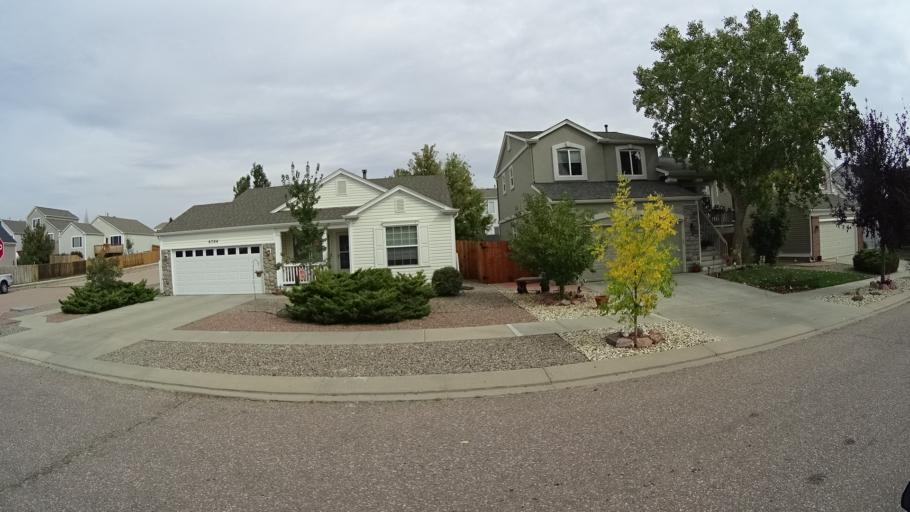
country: US
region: Colorado
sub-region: El Paso County
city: Cimarron Hills
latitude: 38.9142
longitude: -104.7033
